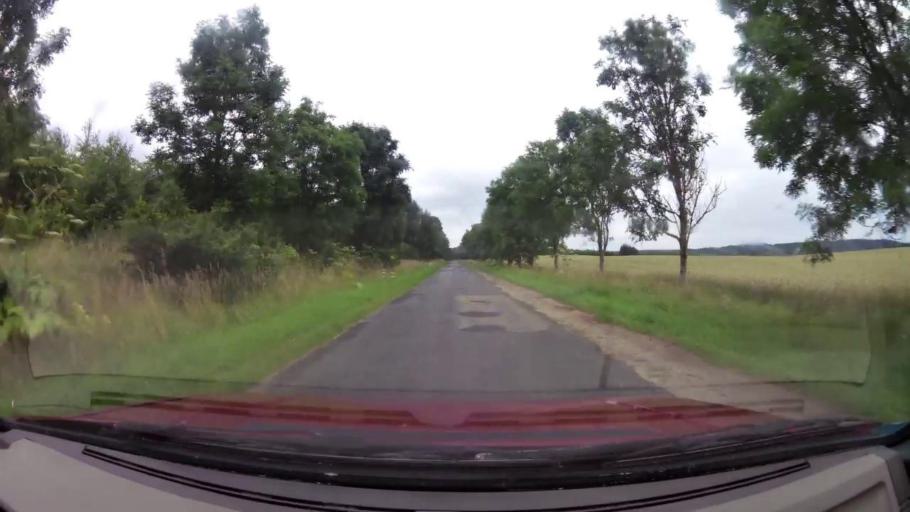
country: PL
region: West Pomeranian Voivodeship
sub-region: Powiat bialogardzki
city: Bialogard
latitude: 53.9398
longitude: 15.9585
